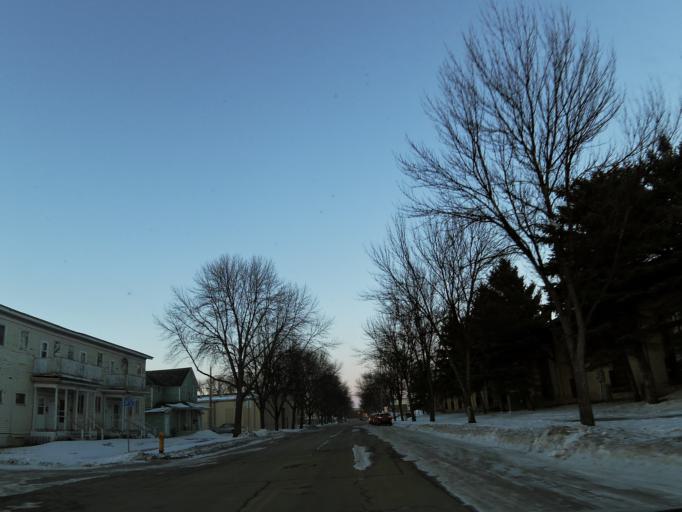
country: US
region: North Dakota
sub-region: Grand Forks County
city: Grand Forks
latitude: 47.9218
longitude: -97.0389
